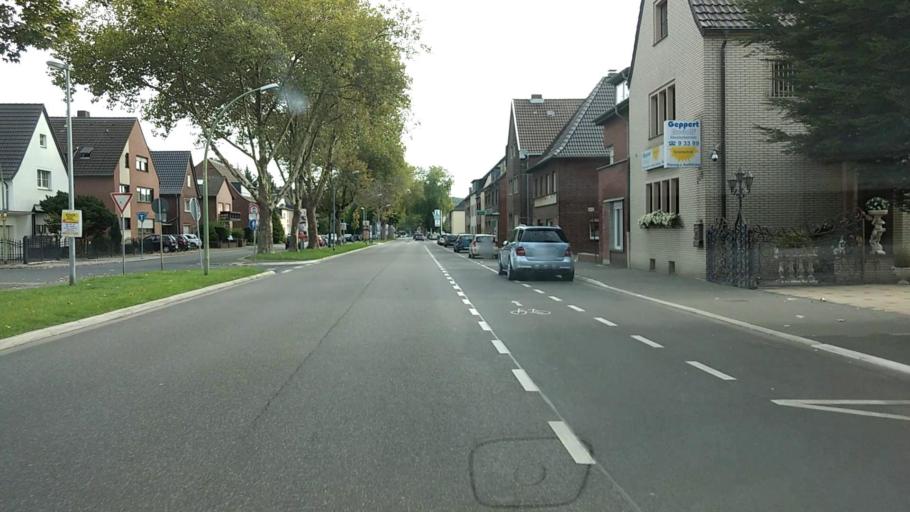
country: DE
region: North Rhine-Westphalia
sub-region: Regierungsbezirk Koln
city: Bergheim
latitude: 50.9382
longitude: 6.6900
